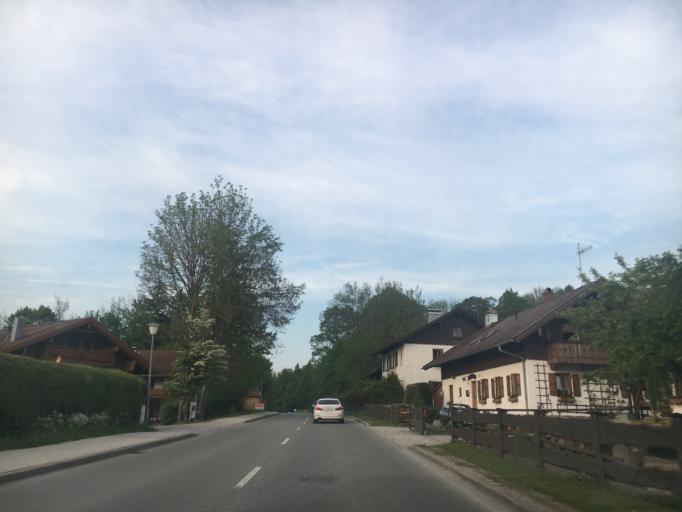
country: DE
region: Bavaria
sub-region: Upper Bavaria
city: Bad Heilbrunn
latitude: 47.7415
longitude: 11.4537
